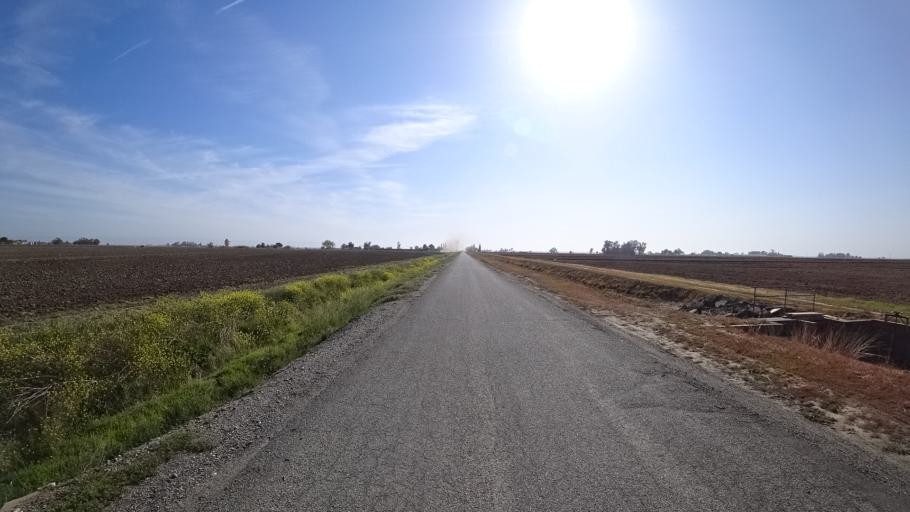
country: US
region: California
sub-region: Glenn County
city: Willows
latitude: 39.5605
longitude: -122.1168
